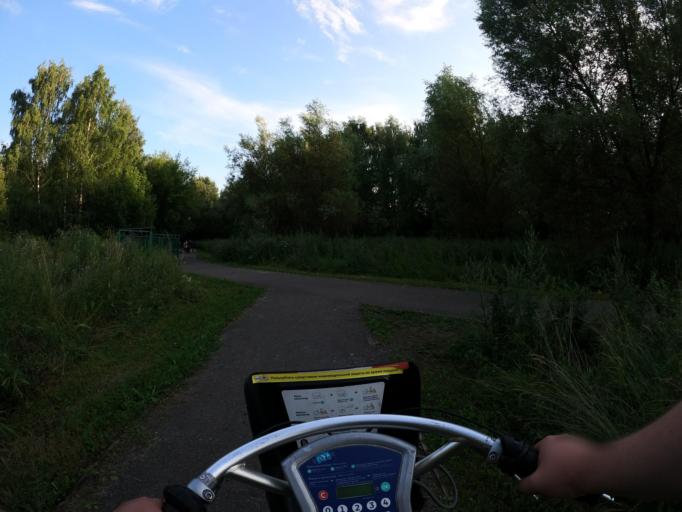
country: RU
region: Moscow
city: Strogino
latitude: 55.8198
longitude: 37.4109
